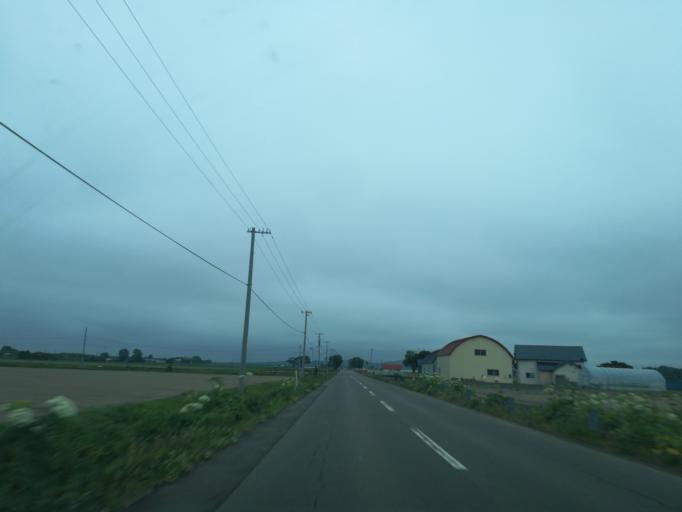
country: JP
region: Hokkaido
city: Iwamizawa
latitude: 43.1391
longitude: 141.7166
